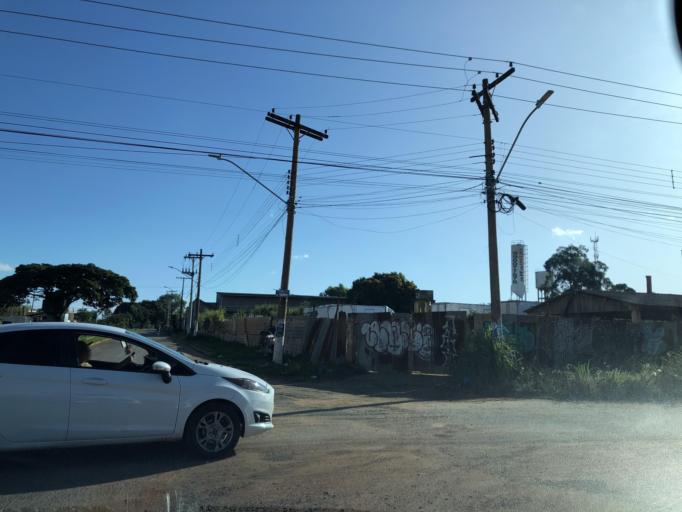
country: BR
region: Goias
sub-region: Luziania
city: Luziania
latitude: -16.1376
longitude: -47.9528
